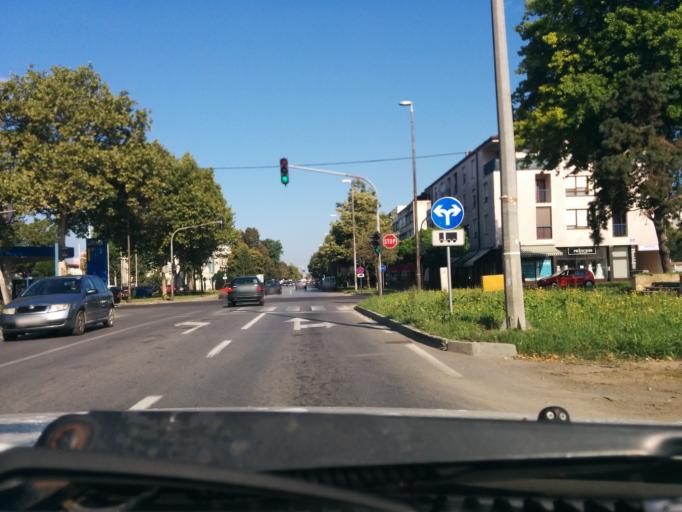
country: HR
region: Sisacko-Moslavacka
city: Kutina
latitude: 45.4777
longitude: 16.7804
